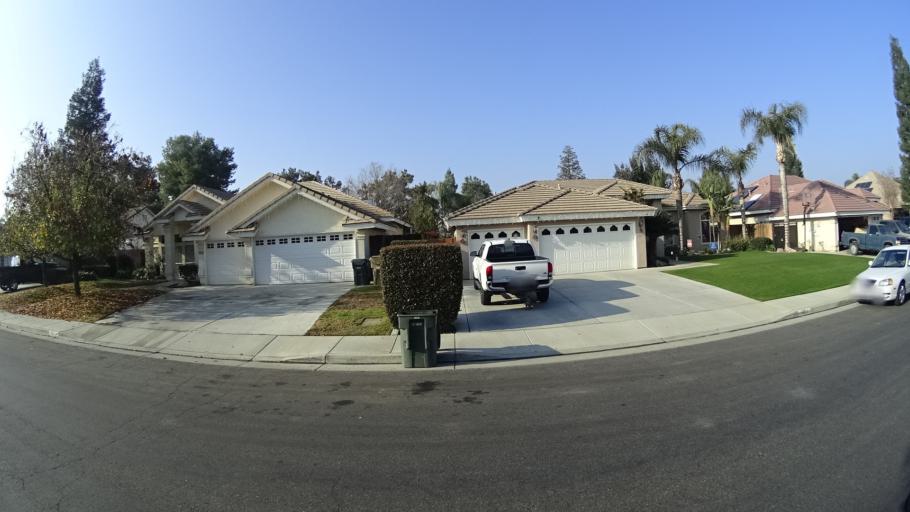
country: US
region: California
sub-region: Kern County
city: Greenacres
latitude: 35.3961
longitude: -119.1043
